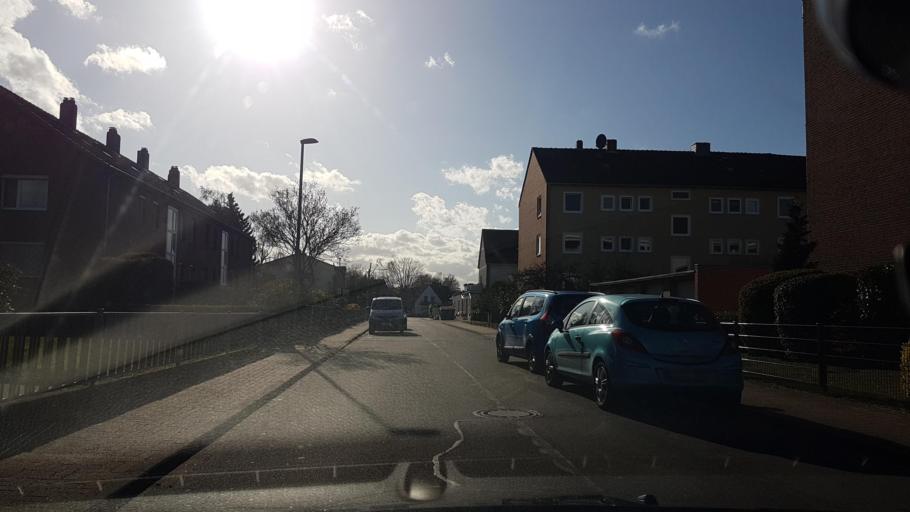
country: DE
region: Lower Saxony
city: Auf der Horst
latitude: 52.4101
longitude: 9.6059
